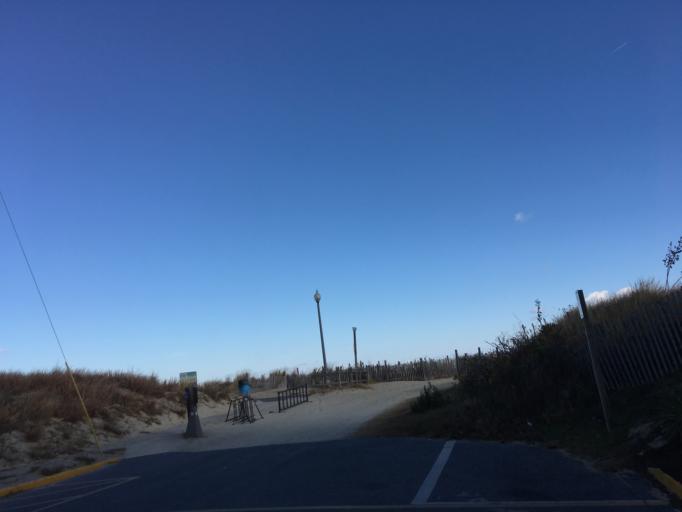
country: US
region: Delaware
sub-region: Sussex County
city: Rehoboth Beach
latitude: 38.7076
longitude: -75.0755
